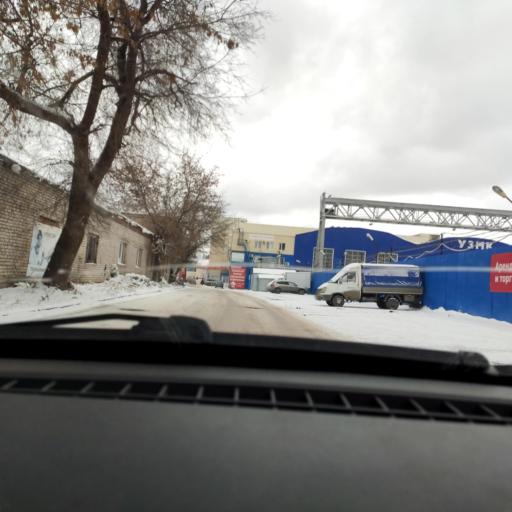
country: RU
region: Bashkortostan
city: Ufa
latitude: 54.8002
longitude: 56.0926
